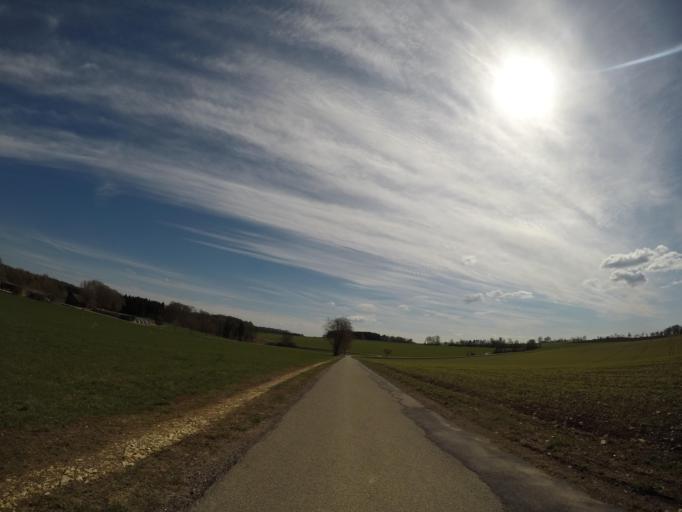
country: DE
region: Baden-Wuerttemberg
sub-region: Tuebingen Region
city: Mehrstetten
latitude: 48.3455
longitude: 9.5706
